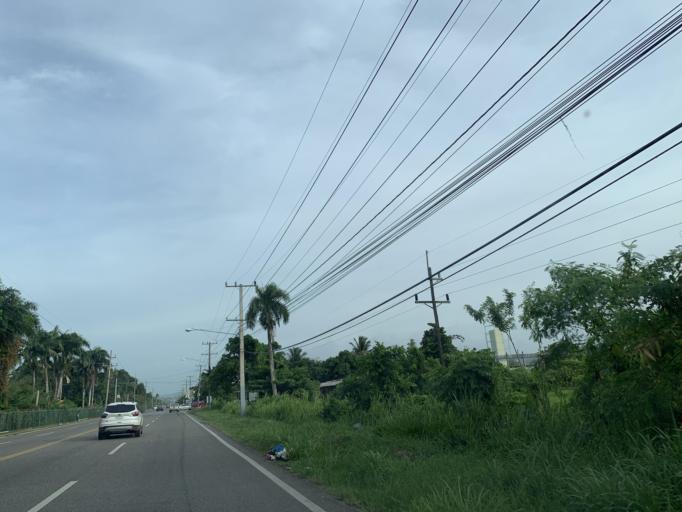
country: DO
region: Puerto Plata
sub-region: Puerto Plata
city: Puerto Plata
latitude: 19.7637
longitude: -70.6488
